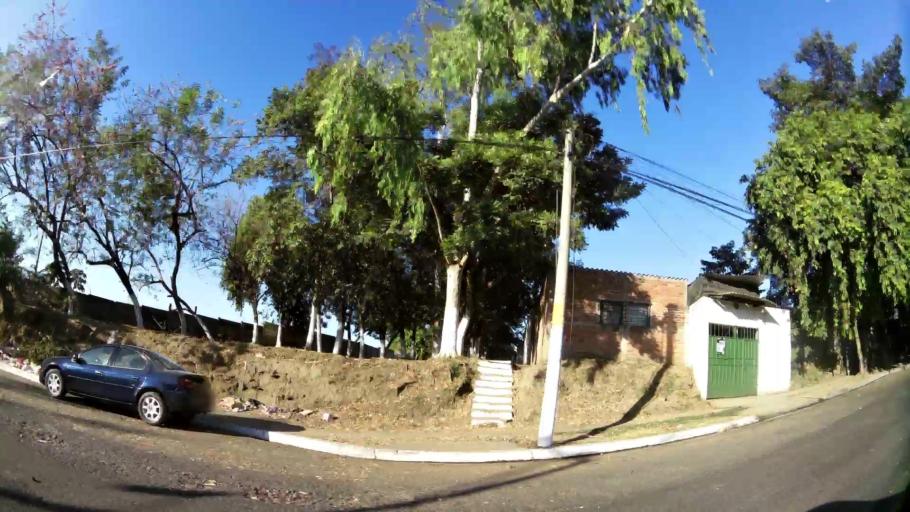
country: SV
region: La Libertad
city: Santa Tecla
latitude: 13.7414
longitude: -89.3579
